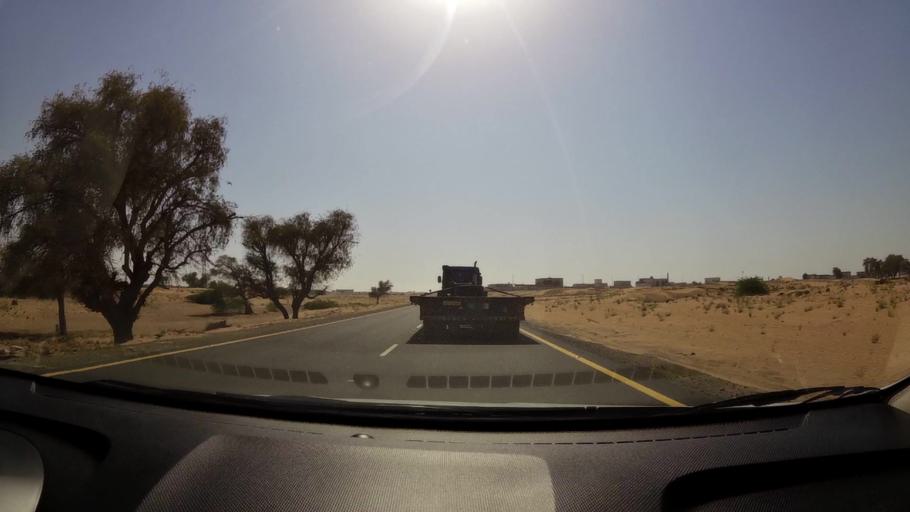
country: AE
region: Umm al Qaywayn
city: Umm al Qaywayn
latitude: 25.4800
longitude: 55.6183
